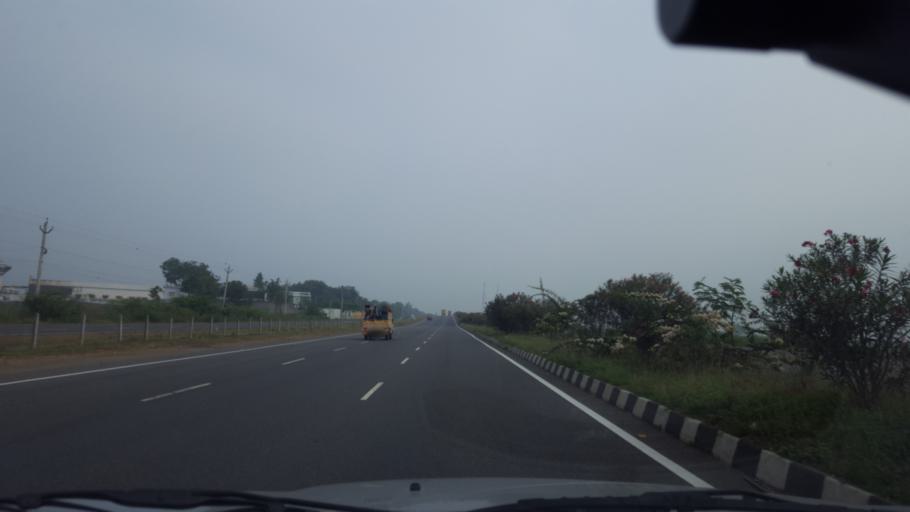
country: IN
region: Andhra Pradesh
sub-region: Guntur
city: Chilakalurupet
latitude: 16.0409
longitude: 80.1362
